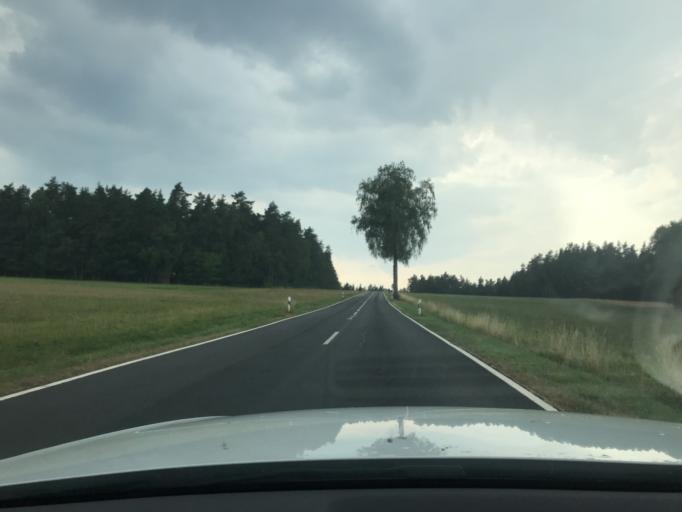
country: DE
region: Bavaria
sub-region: Upper Franconia
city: Prebitz
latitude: 49.7944
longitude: 11.6751
